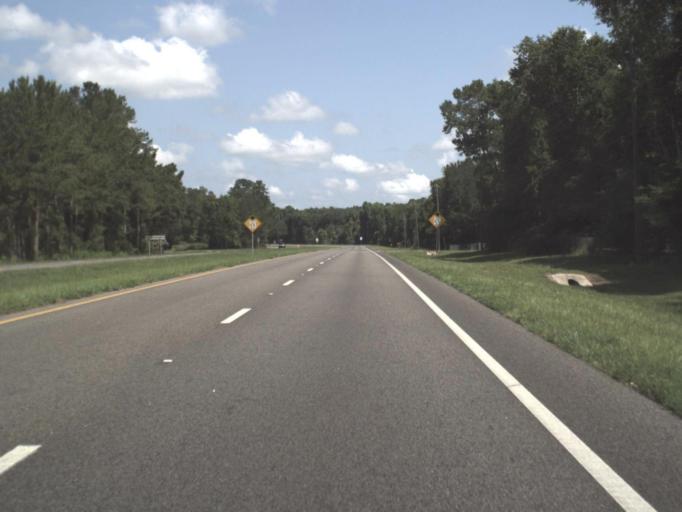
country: US
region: Florida
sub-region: Alachua County
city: Gainesville
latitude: 29.5057
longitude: -82.2679
